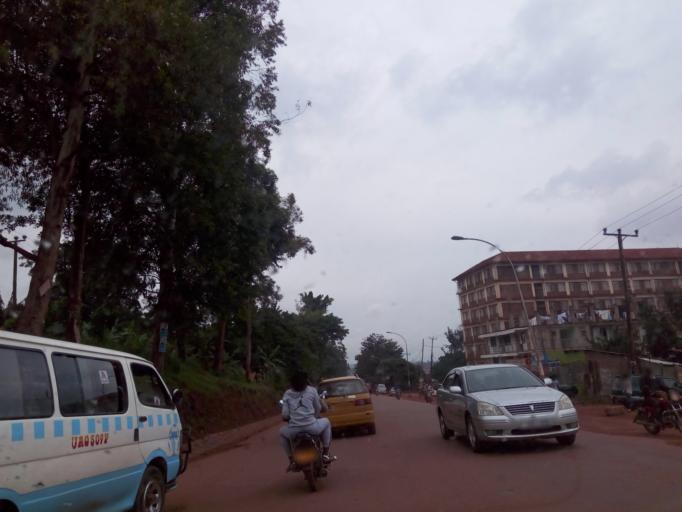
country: UG
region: Central Region
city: Kampala Central Division
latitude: 0.3348
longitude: 32.5639
